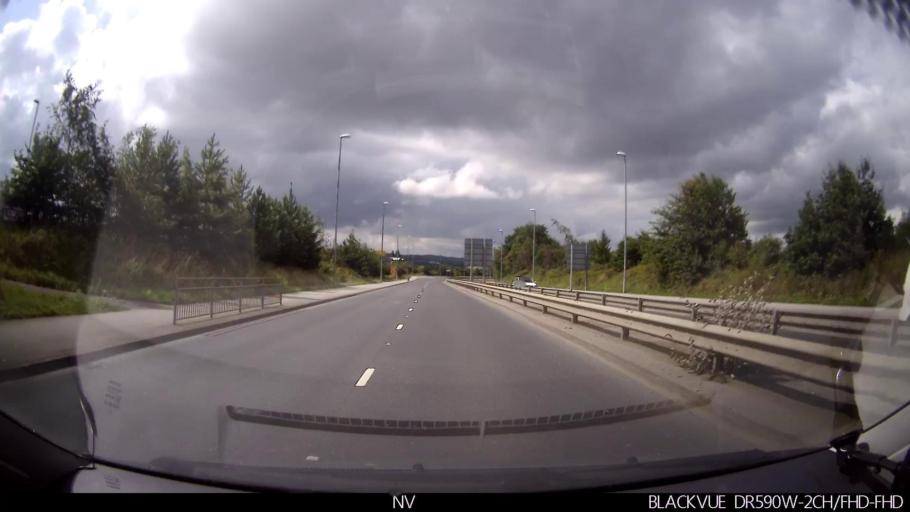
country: GB
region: England
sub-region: City and Borough of Leeds
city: Leeds
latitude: 53.7876
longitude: -1.5135
